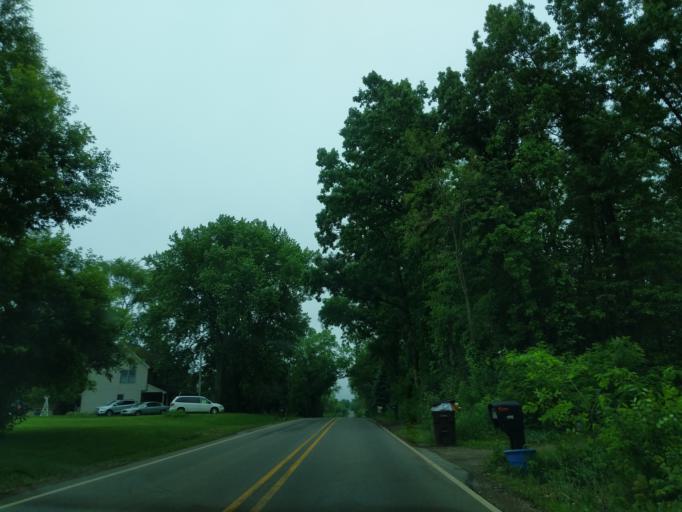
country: US
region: Michigan
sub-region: Jackson County
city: Spring Arbor
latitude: 42.2156
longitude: -84.5703
